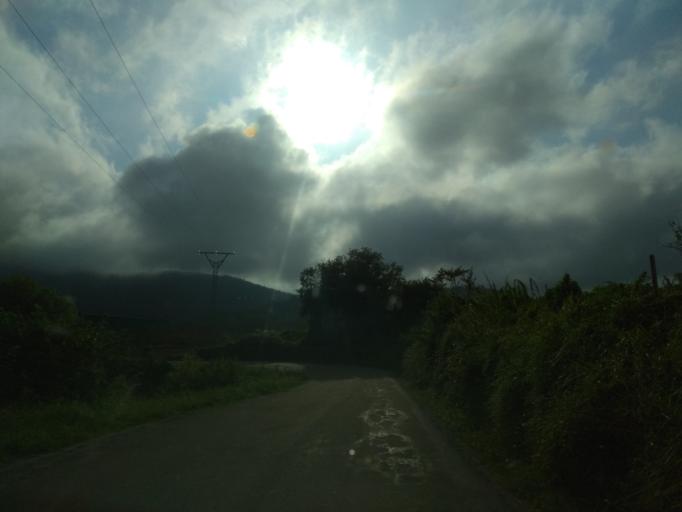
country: ES
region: Cantabria
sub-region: Provincia de Cantabria
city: San Vicente de la Barquera
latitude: 43.3116
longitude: -4.3903
